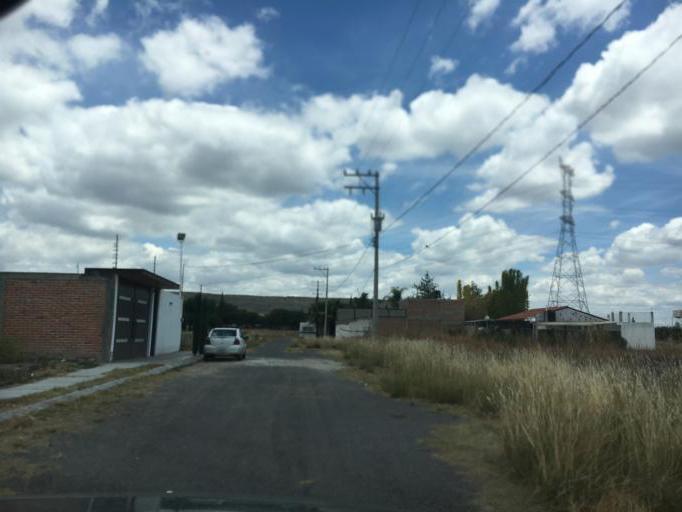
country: MX
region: Guanajuato
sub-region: San Francisco del Rincon
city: Barrio de Guadalupe del Mezquitillo
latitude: 20.9264
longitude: -101.7516
